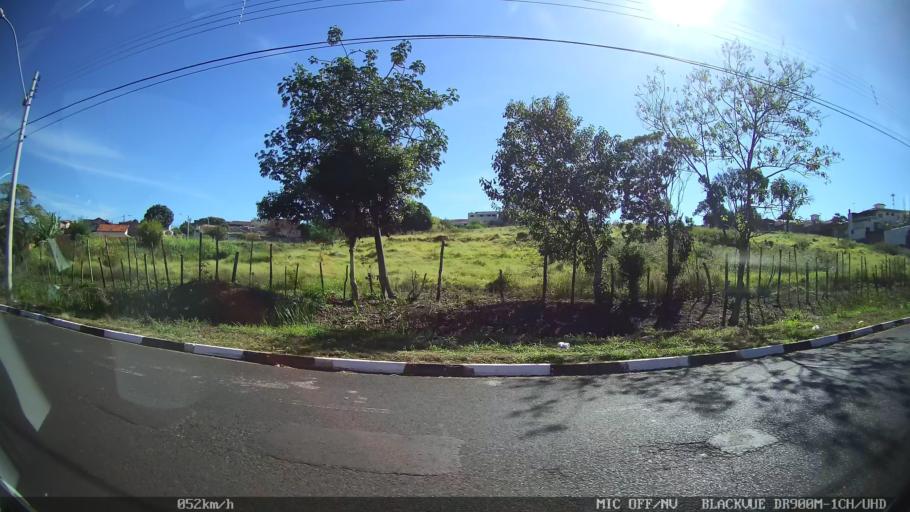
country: BR
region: Sao Paulo
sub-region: Franca
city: Franca
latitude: -20.5195
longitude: -47.3866
